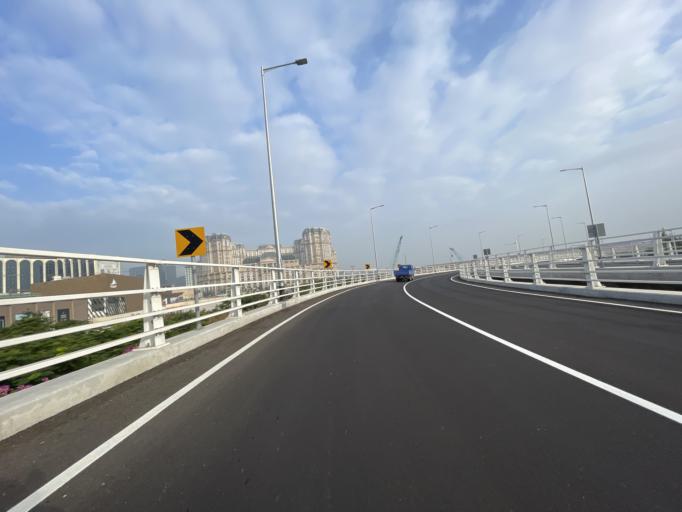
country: MO
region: Macau
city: Macau
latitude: 22.1386
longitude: 113.5756
